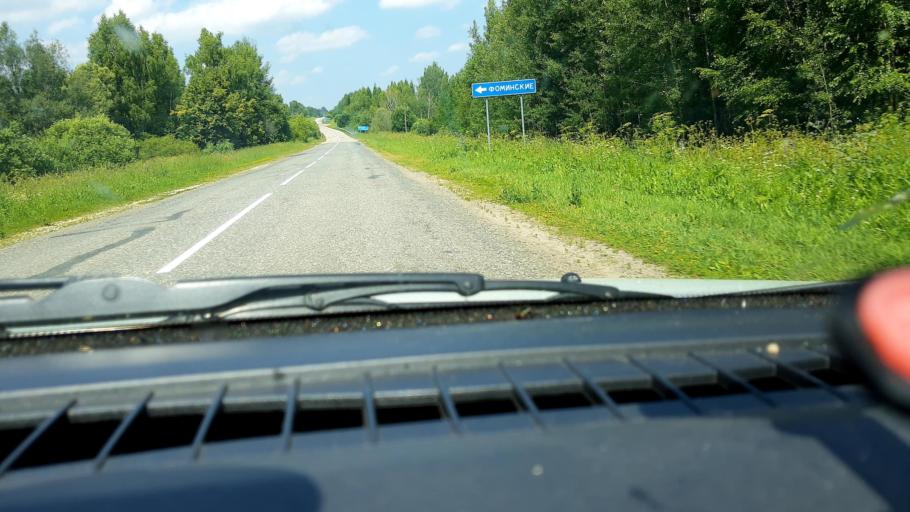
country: RU
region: Nizjnij Novgorod
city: Sharanga
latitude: 57.0776
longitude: 46.5383
